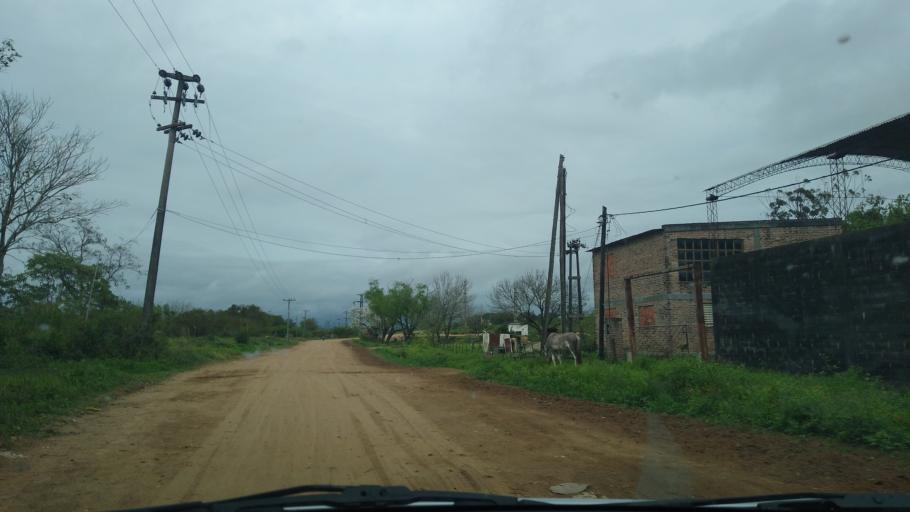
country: AR
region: Chaco
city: Barranqueras
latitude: -27.4746
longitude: -58.9128
